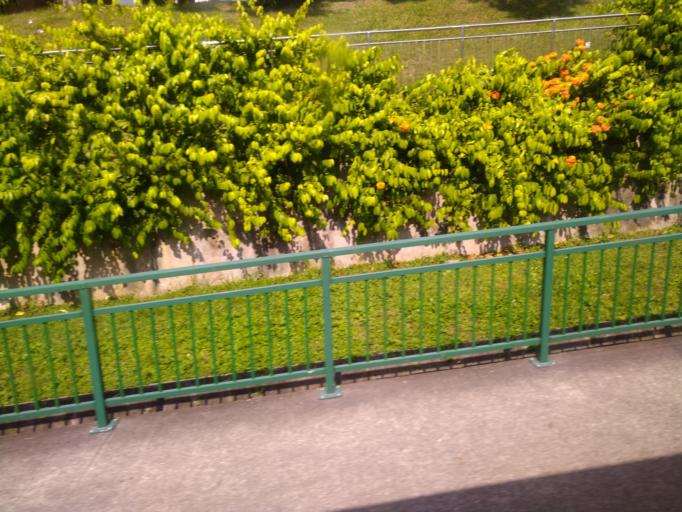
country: SG
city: Singapore
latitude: 1.2891
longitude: 103.8129
